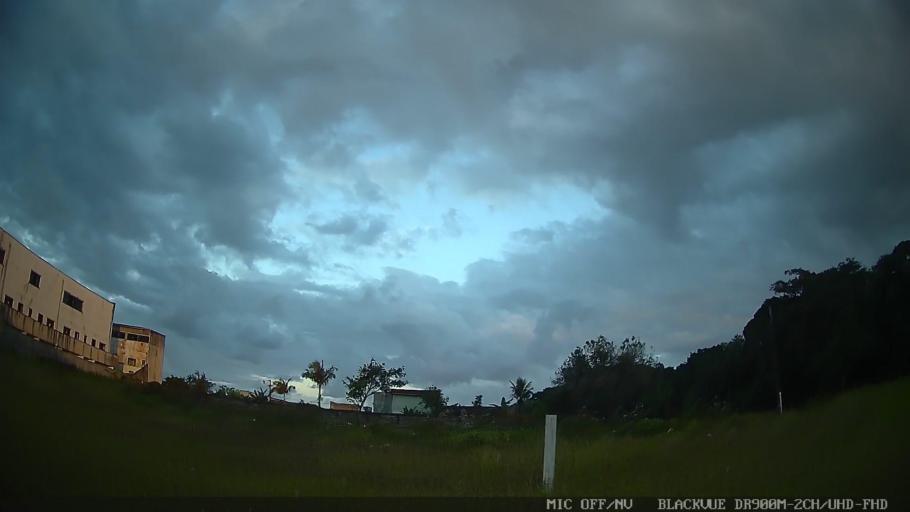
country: BR
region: Sao Paulo
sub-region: Itanhaem
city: Itanhaem
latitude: -24.1874
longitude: -46.8363
